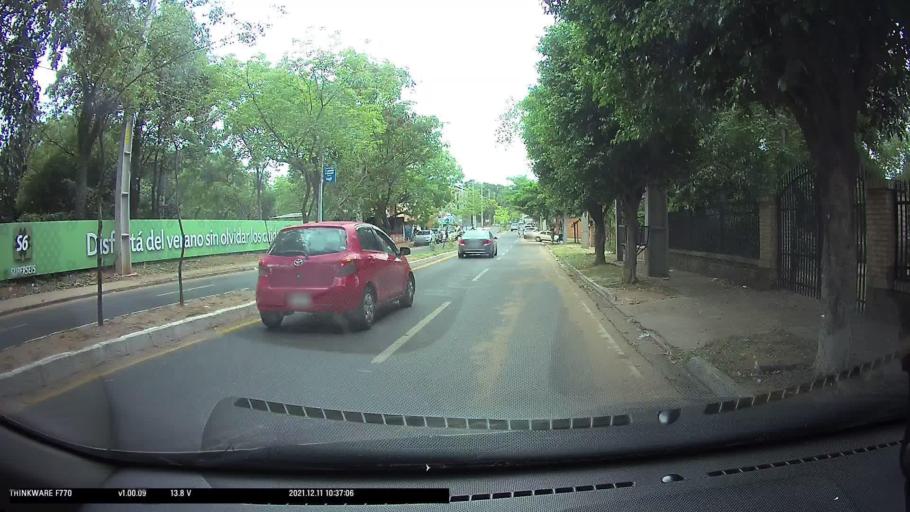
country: PY
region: Cordillera
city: San Bernardino
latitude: -25.3052
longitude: -57.2953
